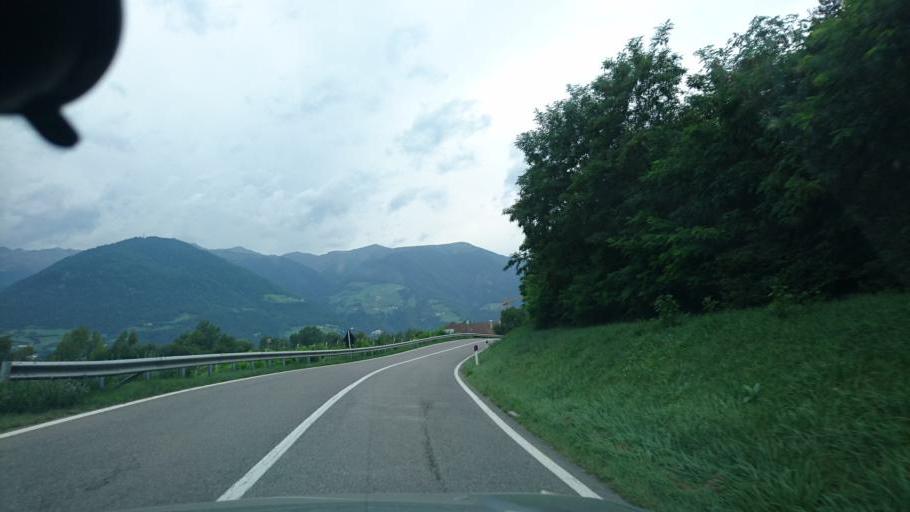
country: IT
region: Trentino-Alto Adige
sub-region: Bolzano
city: Prato Allo Stelvio
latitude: 46.6326
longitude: 10.6187
